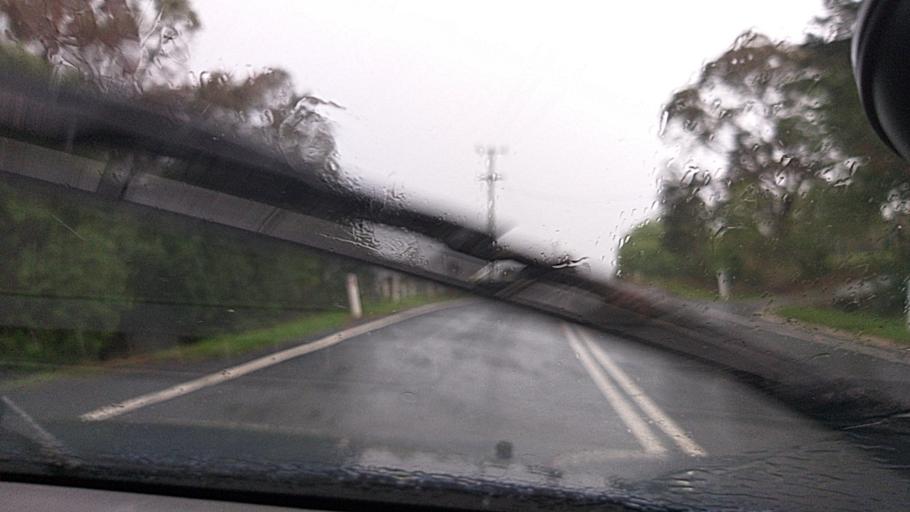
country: AU
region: New South Wales
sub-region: Wollondilly
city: Douglas Park
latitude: -34.1732
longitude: 150.7145
